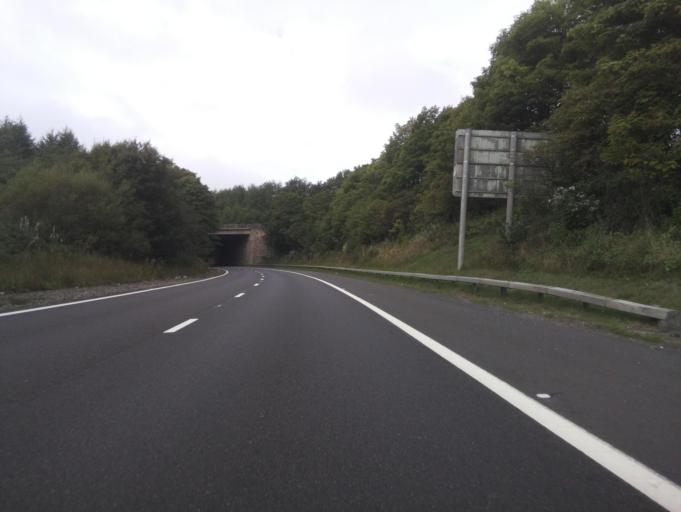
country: GB
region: Scotland
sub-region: Falkirk
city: Denny
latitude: 56.0028
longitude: -3.9147
